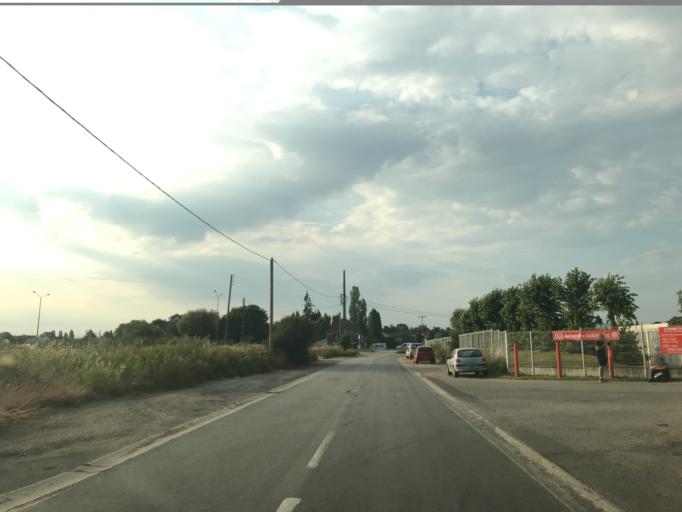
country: FR
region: Ile-de-France
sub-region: Departement des Yvelines
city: Les Essarts-le-Roi
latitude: 48.7240
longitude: 1.8881
